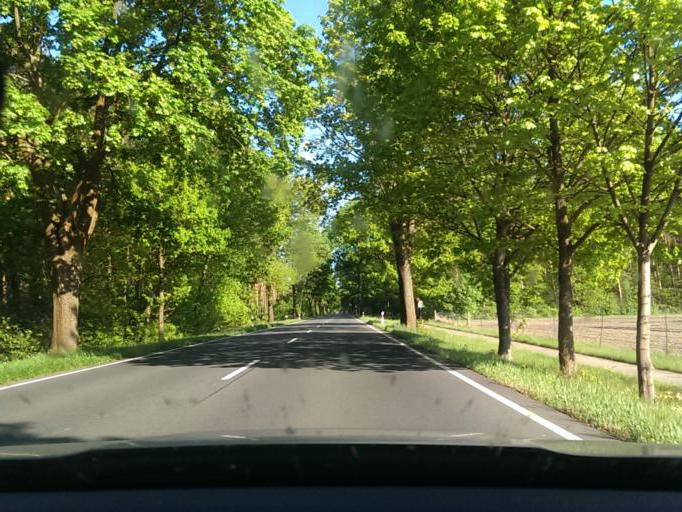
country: DE
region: Lower Saxony
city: Wietze
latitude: 52.6437
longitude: 9.8752
